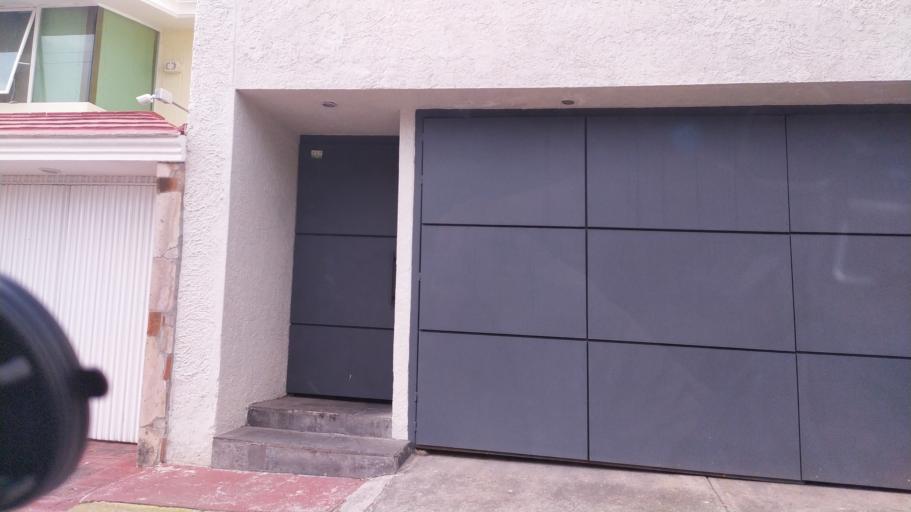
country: MX
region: Jalisco
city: Zapopan2
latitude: 20.7014
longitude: -103.4079
